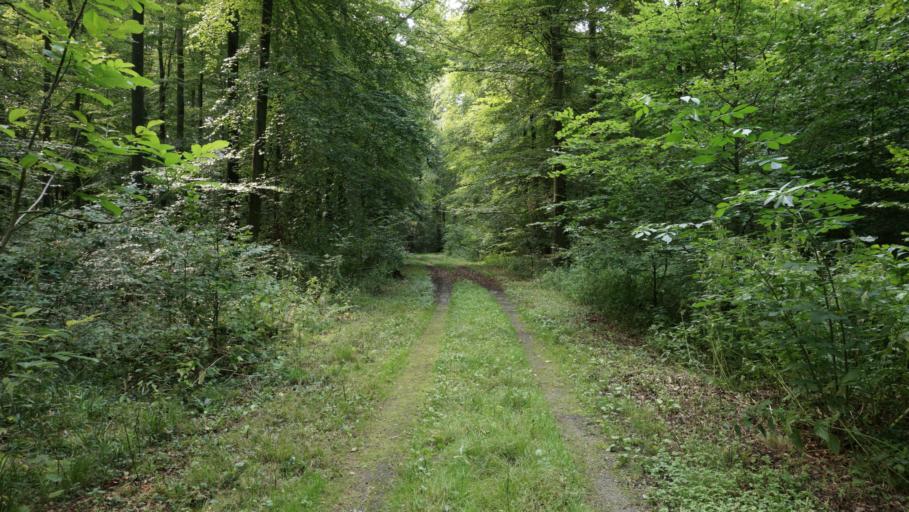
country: DE
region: Baden-Wuerttemberg
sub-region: Karlsruhe Region
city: Neckarzimmern
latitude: 49.3305
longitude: 9.1354
